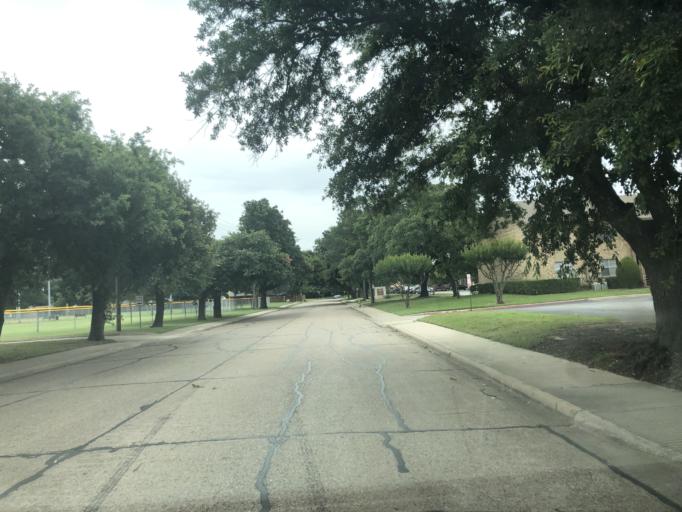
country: US
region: Texas
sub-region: Dallas County
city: Irving
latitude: 32.8014
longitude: -96.9861
